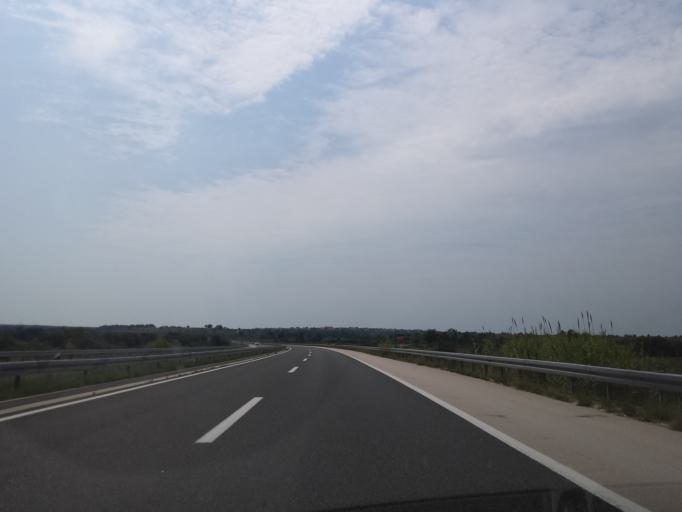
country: HR
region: Zadarska
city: Policnik
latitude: 44.1711
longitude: 15.4232
